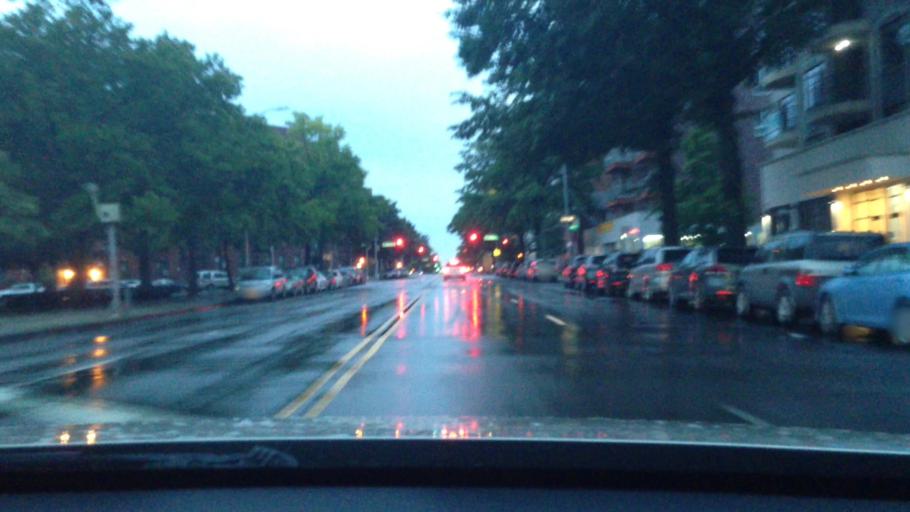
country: US
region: New York
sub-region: Kings County
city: Bensonhurst
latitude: 40.6080
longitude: -73.9875
